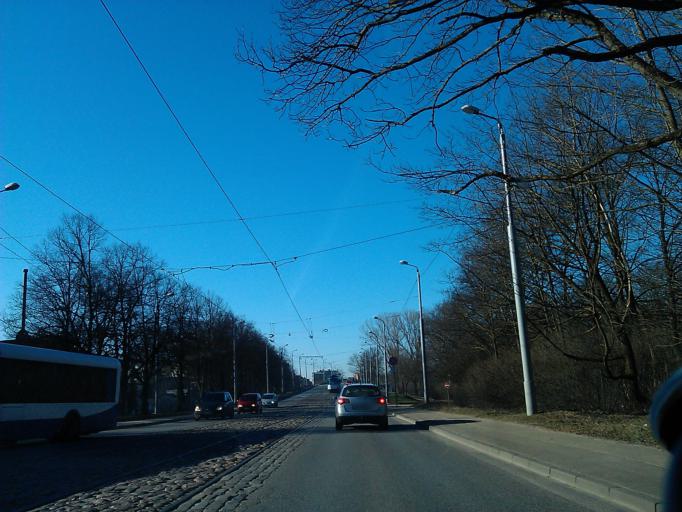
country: LV
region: Riga
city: Riga
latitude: 56.9810
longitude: 24.1484
